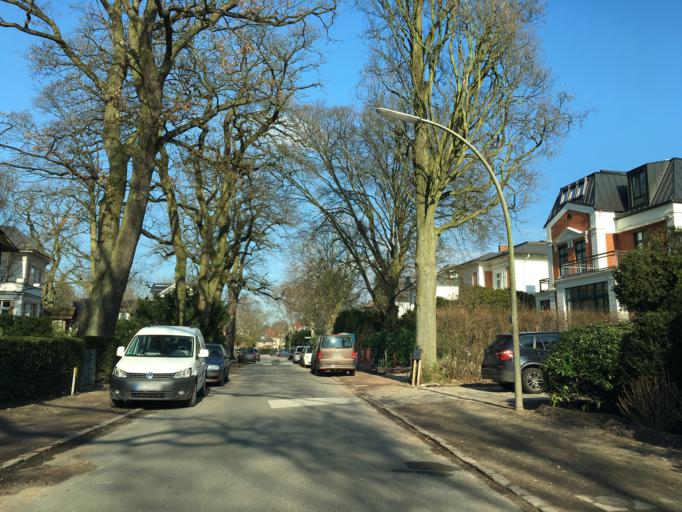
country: DE
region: Hamburg
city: Eidelstedt
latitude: 53.5600
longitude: 9.8782
